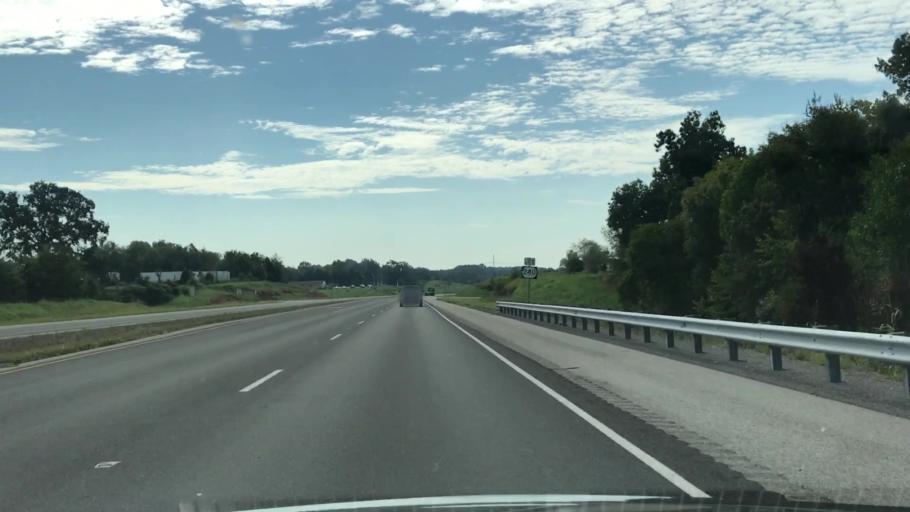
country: US
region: Kentucky
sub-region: Warren County
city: Plano
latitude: 36.8369
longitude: -86.3192
